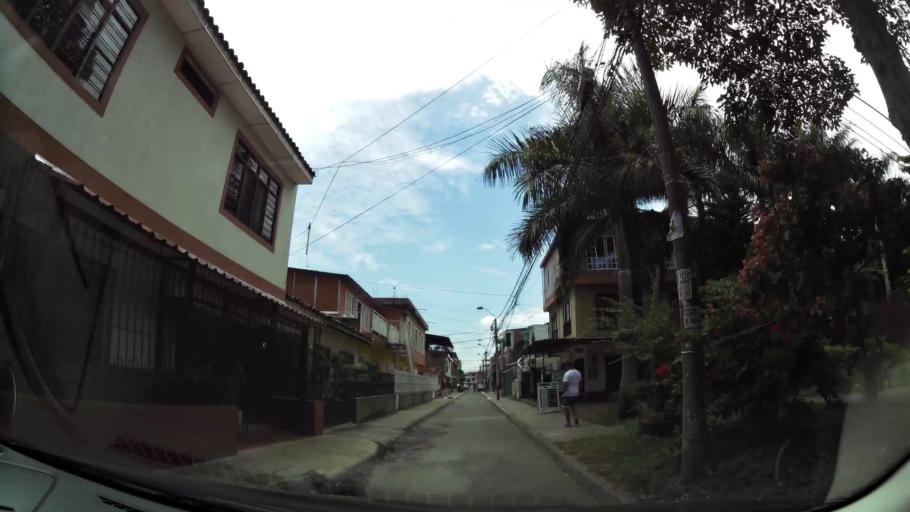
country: CO
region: Valle del Cauca
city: Cali
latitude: 3.4481
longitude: -76.4877
